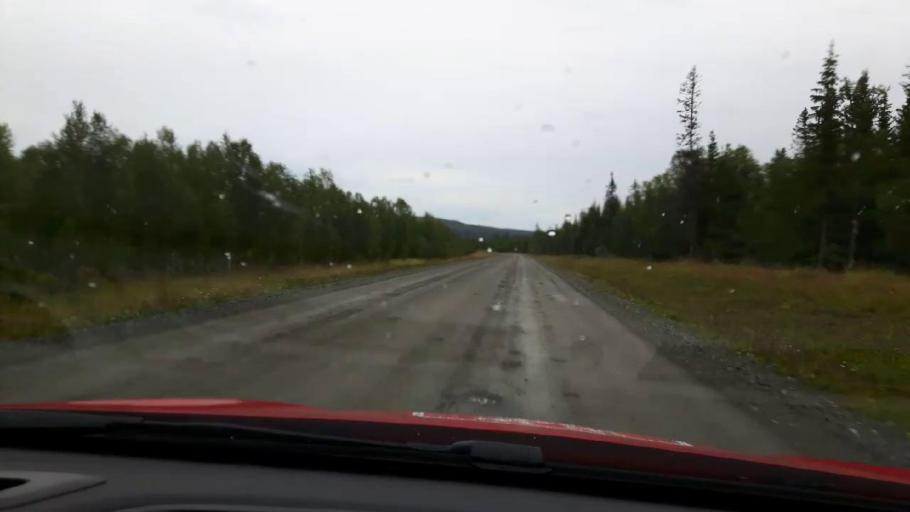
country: NO
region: Nord-Trondelag
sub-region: Meraker
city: Meraker
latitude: 63.5568
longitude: 12.3182
